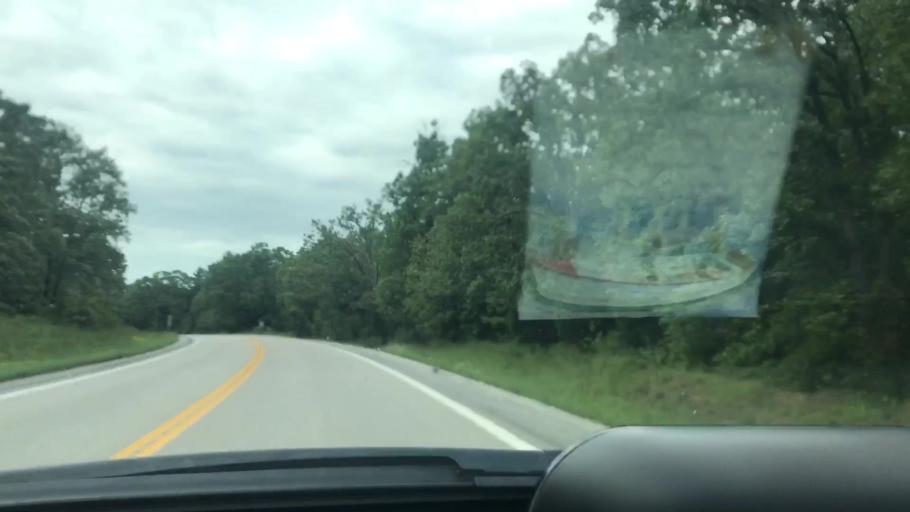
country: US
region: Missouri
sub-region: Benton County
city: Warsaw
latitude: 38.1610
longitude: -93.2987
